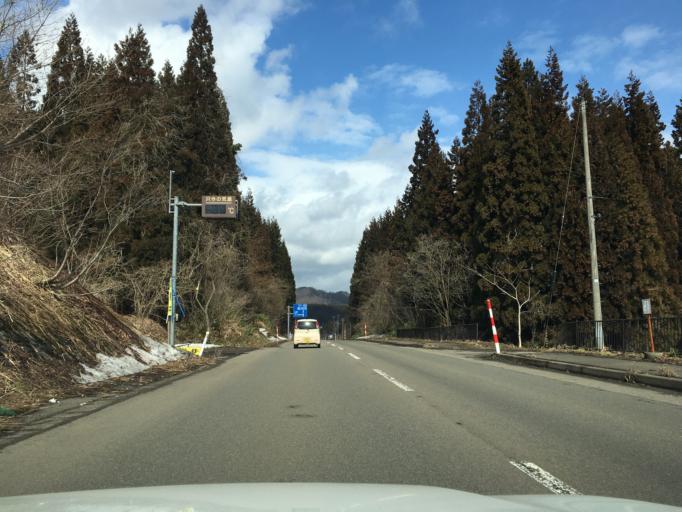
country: JP
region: Akita
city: Takanosu
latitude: 40.0211
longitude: 140.2749
